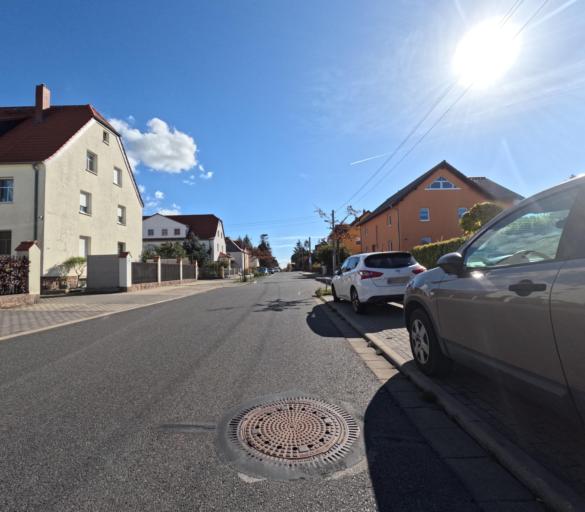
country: DE
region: Saxony
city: Albertstadt
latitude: 51.1171
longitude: 13.7244
